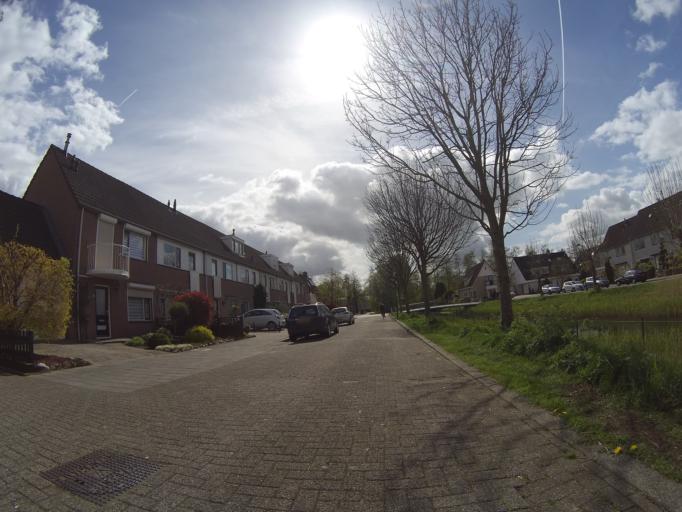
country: NL
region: Utrecht
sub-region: Gemeente Veenendaal
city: Veenendaal
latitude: 52.0303
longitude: 5.5283
